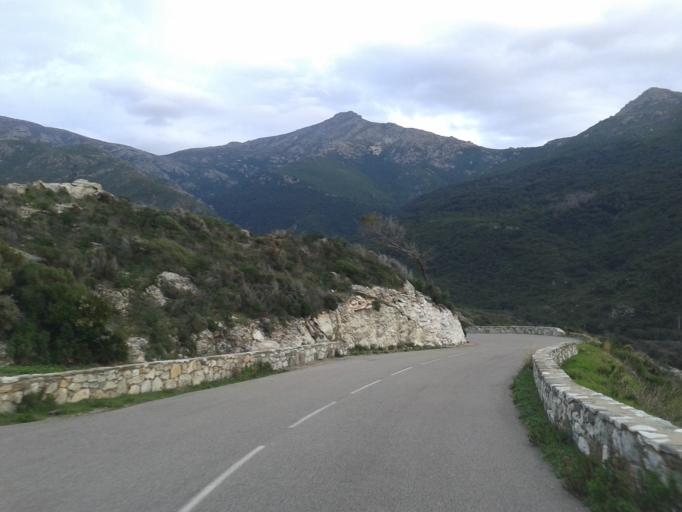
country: FR
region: Corsica
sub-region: Departement de la Haute-Corse
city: Brando
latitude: 42.8695
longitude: 9.3467
